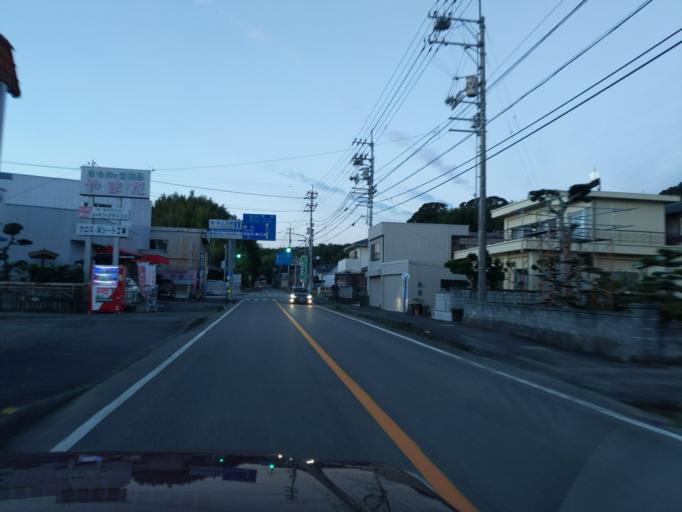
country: JP
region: Tokushima
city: Anan
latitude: 33.8421
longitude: 134.6235
